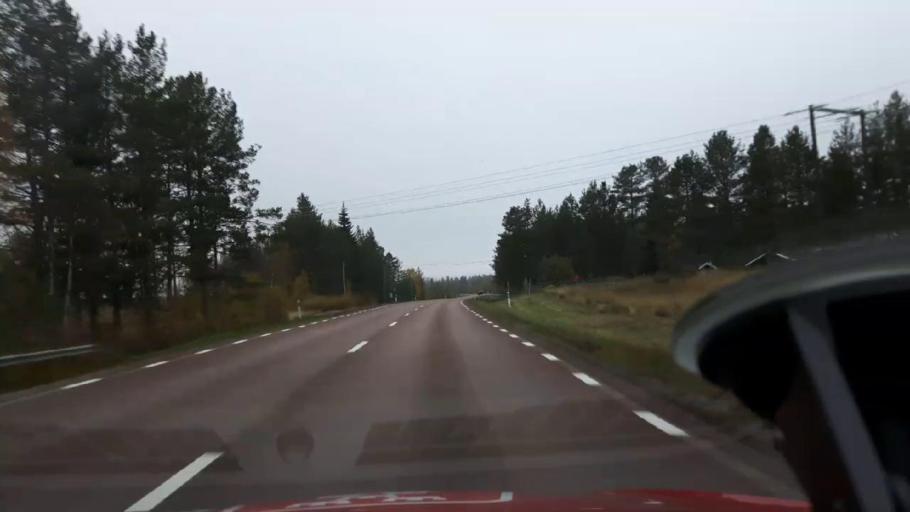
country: SE
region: Jaemtland
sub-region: Bergs Kommun
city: Hoverberg
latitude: 62.5147
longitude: 14.4498
